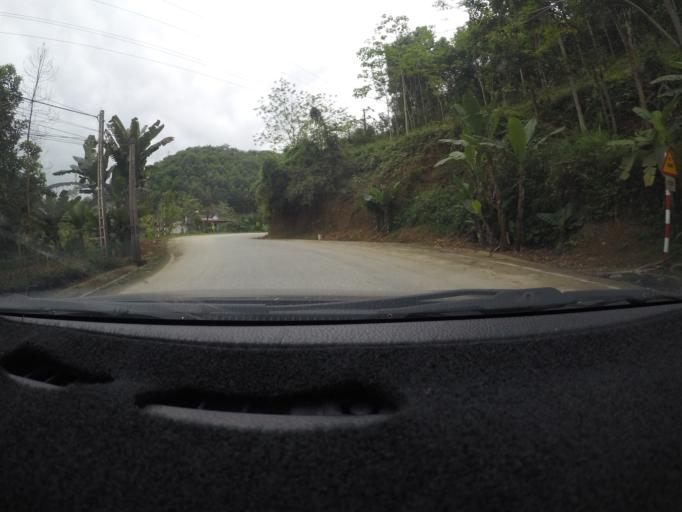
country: VN
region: Yen Bai
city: Thi Tran Yen The
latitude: 21.9323
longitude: 104.7900
